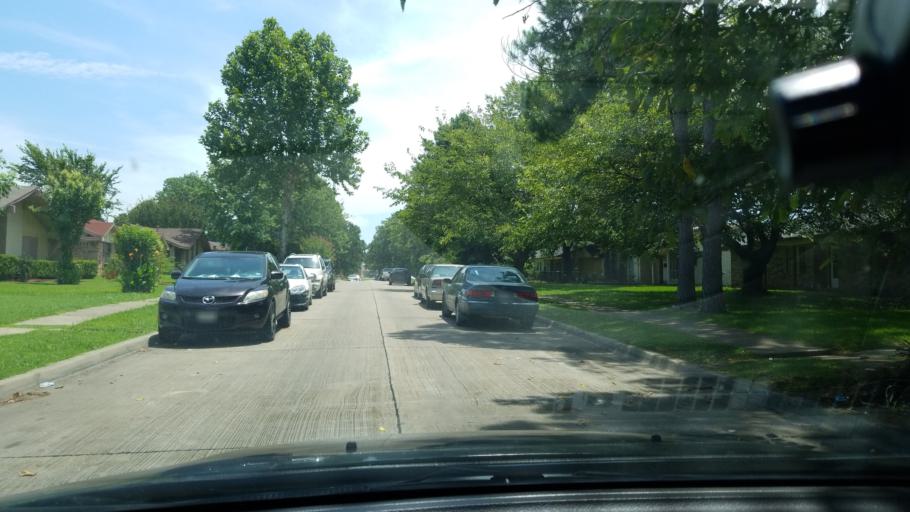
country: US
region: Texas
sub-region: Dallas County
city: Balch Springs
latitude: 32.7408
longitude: -96.6459
